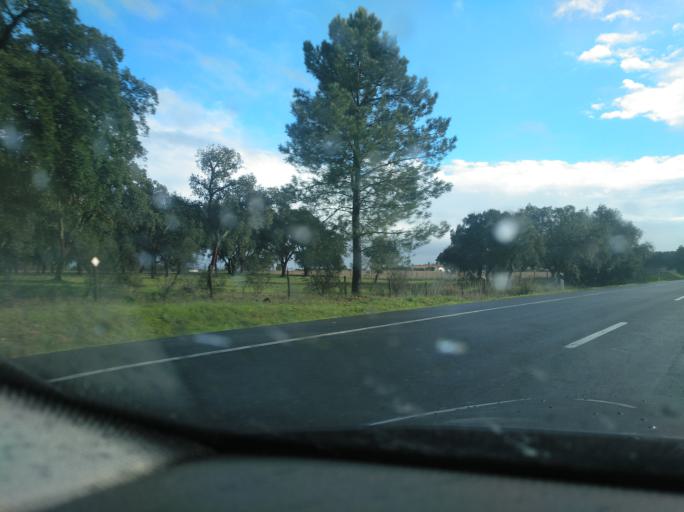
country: PT
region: Setubal
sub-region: Grandola
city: Grandola
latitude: 38.0402
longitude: -8.4011
